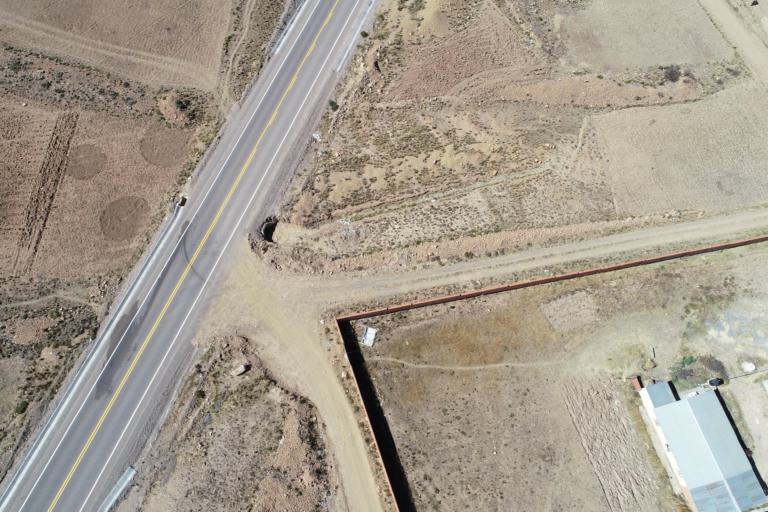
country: BO
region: La Paz
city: Achacachi
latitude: -15.8853
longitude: -68.8119
